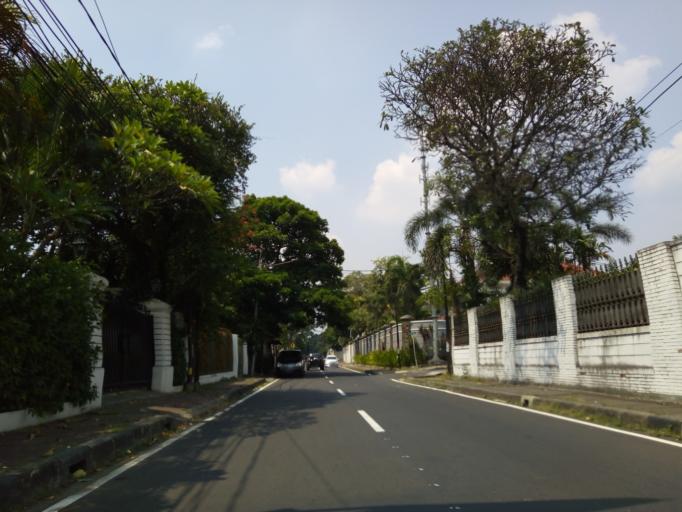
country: ID
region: Jakarta Raya
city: Jakarta
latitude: -6.2018
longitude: 106.8351
